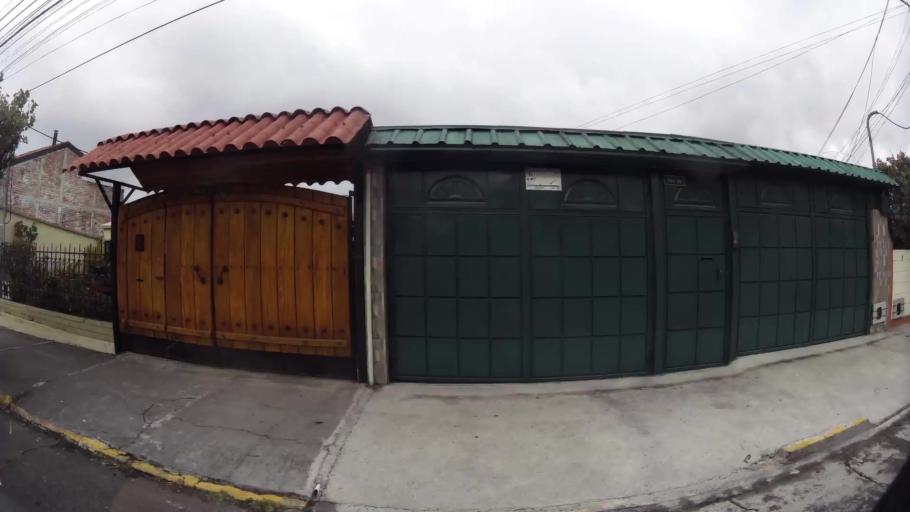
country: EC
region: Pichincha
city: Quito
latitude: -0.1185
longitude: -78.5009
